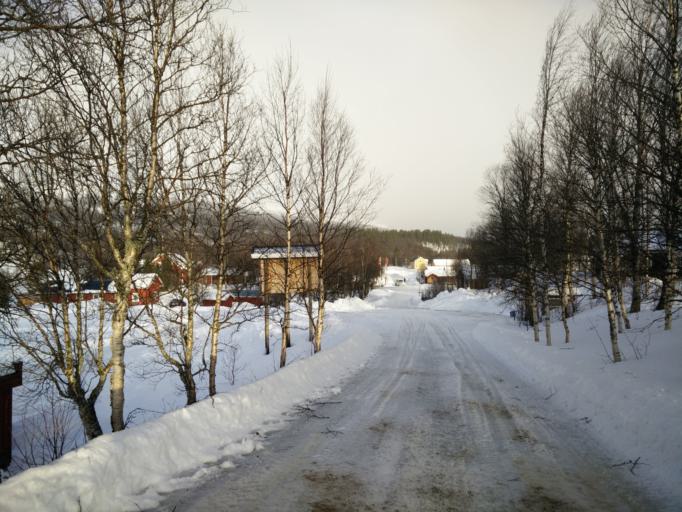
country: NO
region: Sor-Trondelag
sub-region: Tydal
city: Aas
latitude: 62.6400
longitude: 12.4180
